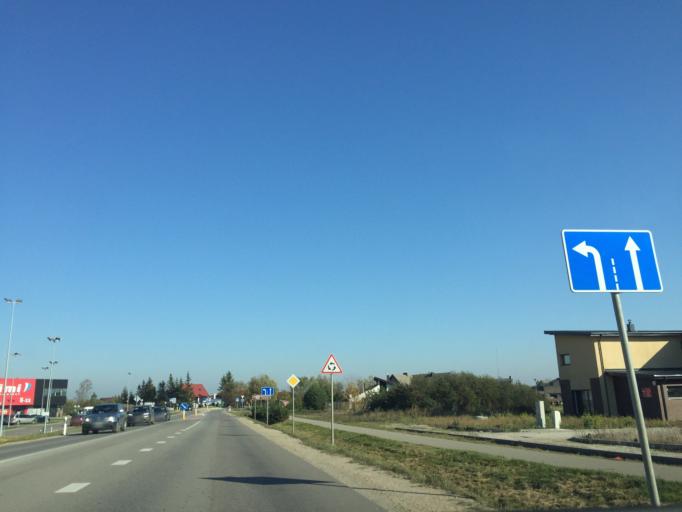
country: LT
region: Klaipedos apskritis
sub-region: Klaipeda
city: Klaipeda
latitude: 55.7355
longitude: 21.1912
